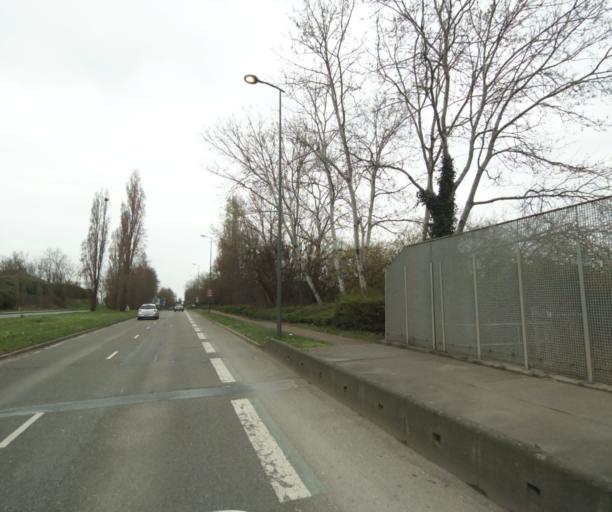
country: FR
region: Ile-de-France
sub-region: Departement du Val-d'Oise
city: Vaureal
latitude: 49.0508
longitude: 2.0239
